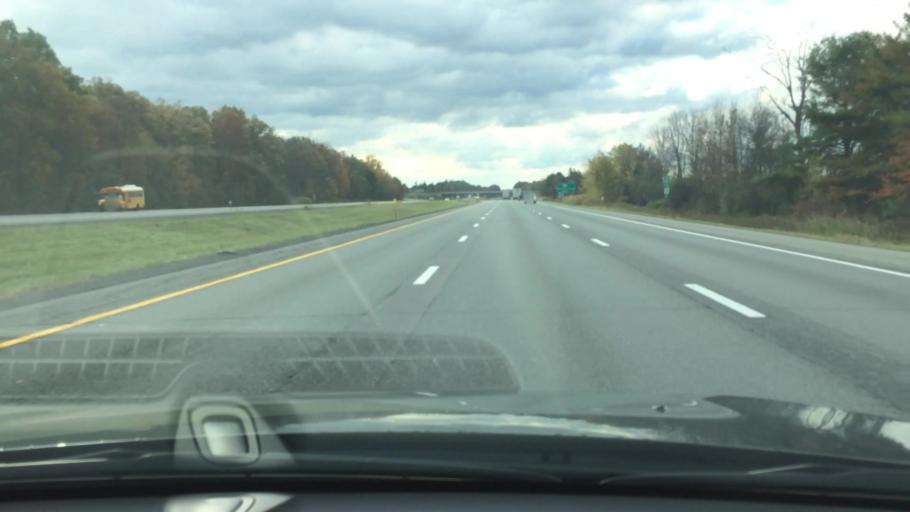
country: US
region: New York
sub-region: Saratoga County
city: Ballston Spa
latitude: 42.9777
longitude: -73.8028
